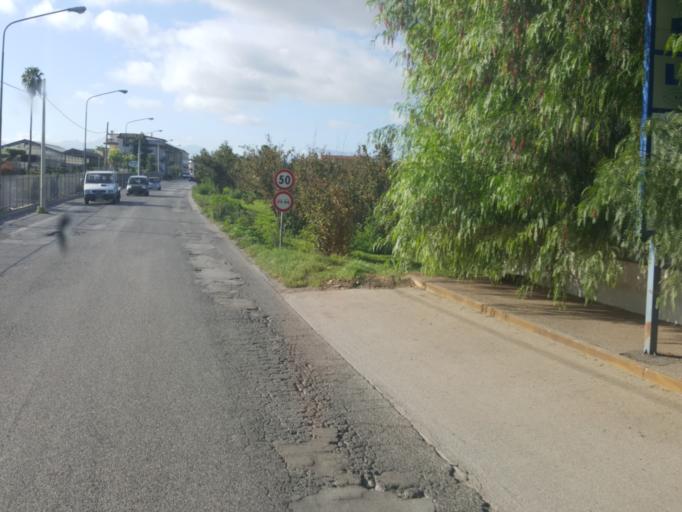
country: IT
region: Campania
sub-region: Provincia di Napoli
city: Nola
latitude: 40.9101
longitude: 14.5279
